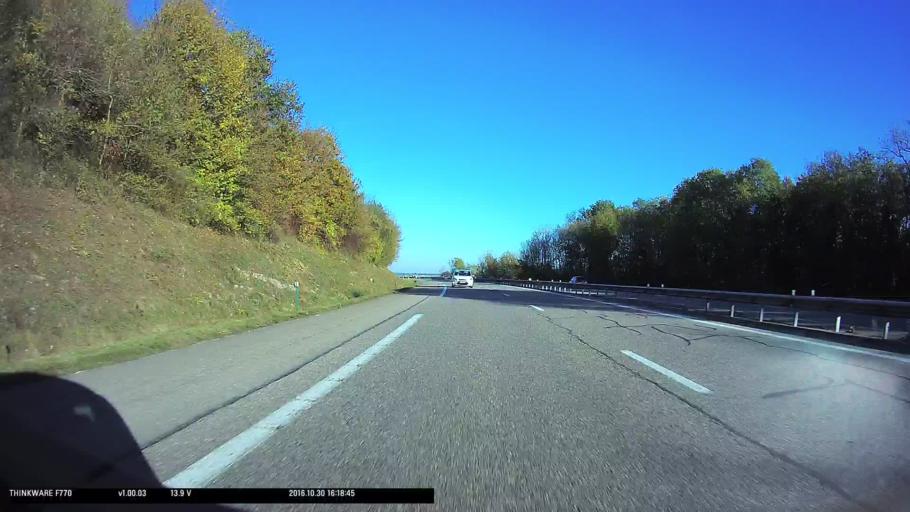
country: FR
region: Franche-Comte
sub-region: Departement du Doubs
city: Clerval
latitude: 47.4057
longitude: 6.4914
